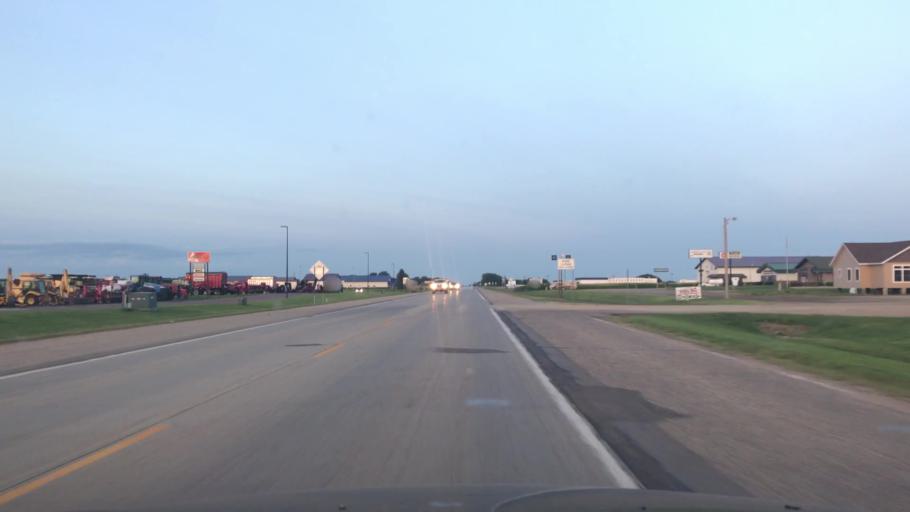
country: US
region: Minnesota
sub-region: Redwood County
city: Redwood Falls
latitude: 44.5414
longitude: -95.0839
